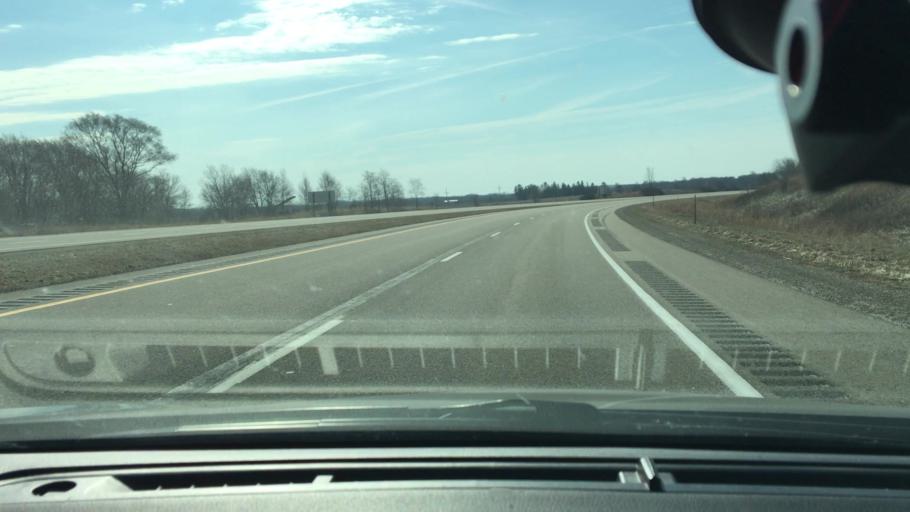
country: US
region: Iowa
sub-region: Floyd County
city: Charles City
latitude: 43.0368
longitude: -92.6542
